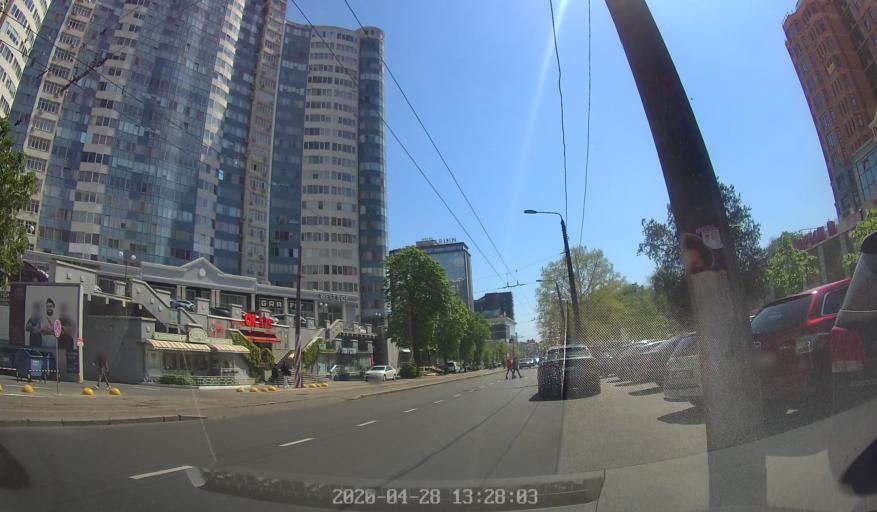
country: NE
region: Zinder
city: Mirriah
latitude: 13.9304
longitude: 9.2279
